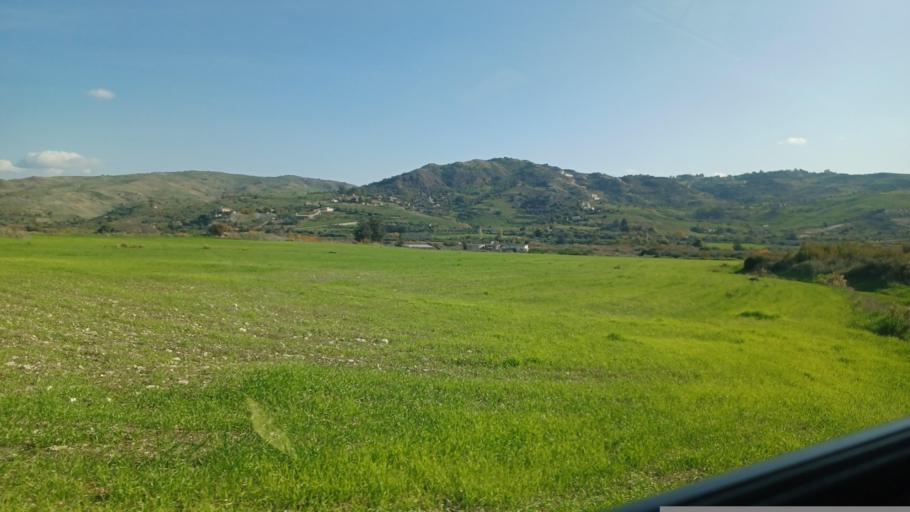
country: CY
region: Pafos
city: Mesogi
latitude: 34.7726
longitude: 32.5743
